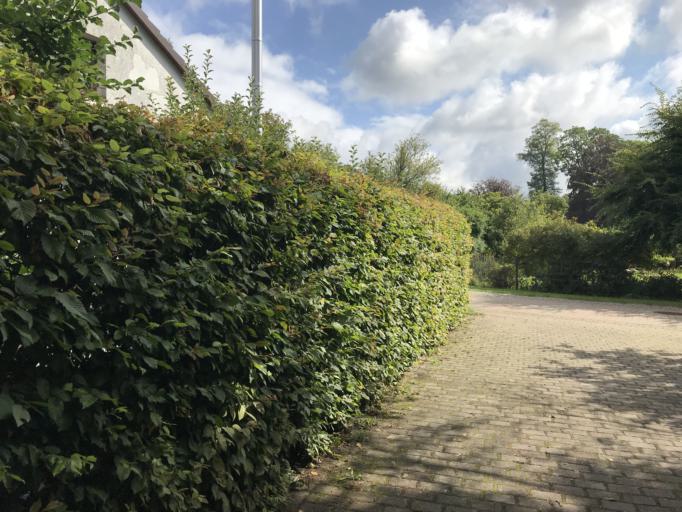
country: DE
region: Lower Saxony
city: Suderburg
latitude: 52.8956
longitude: 10.4525
